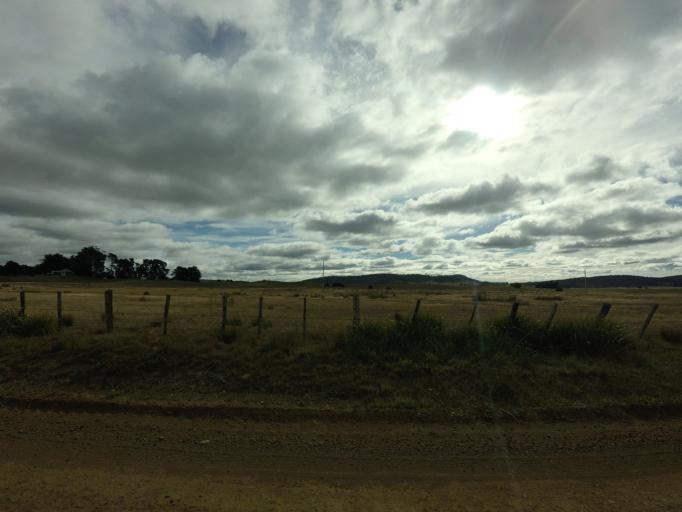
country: AU
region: Tasmania
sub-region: Brighton
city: Bridgewater
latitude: -42.4290
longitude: 147.3884
